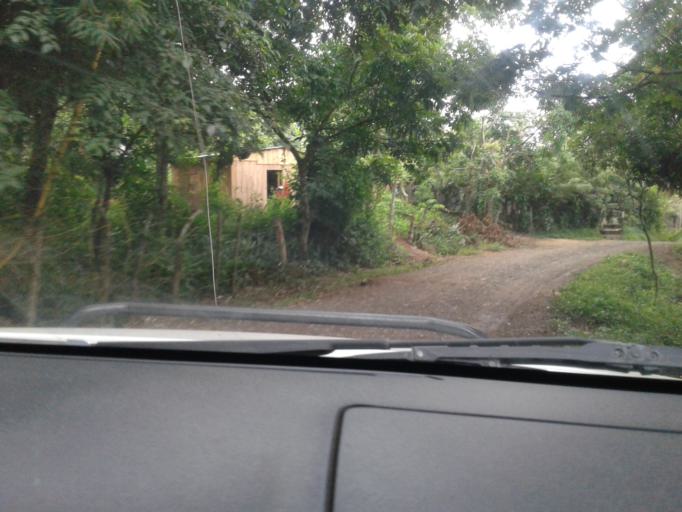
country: NI
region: Matagalpa
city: San Ramon
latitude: 12.9077
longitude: -85.7354
